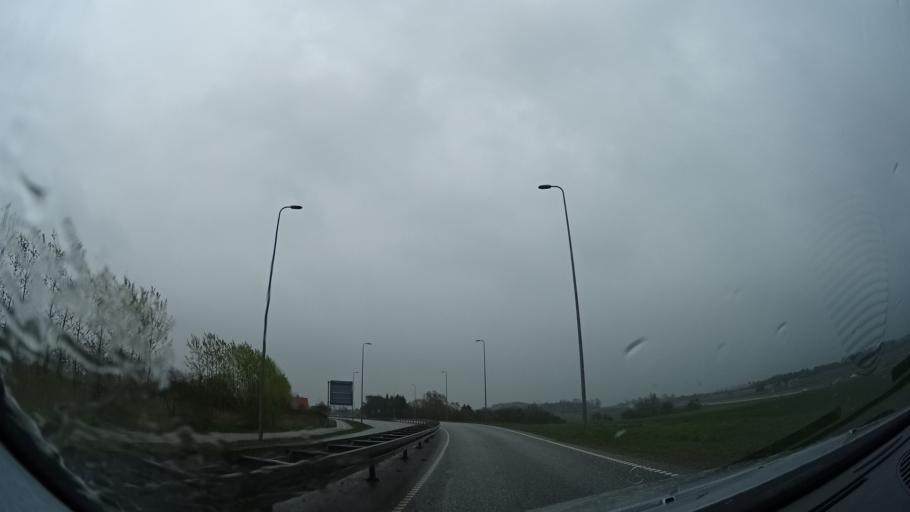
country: DK
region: Zealand
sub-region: Holbaek Kommune
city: Holbaek
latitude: 55.7104
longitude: 11.6383
